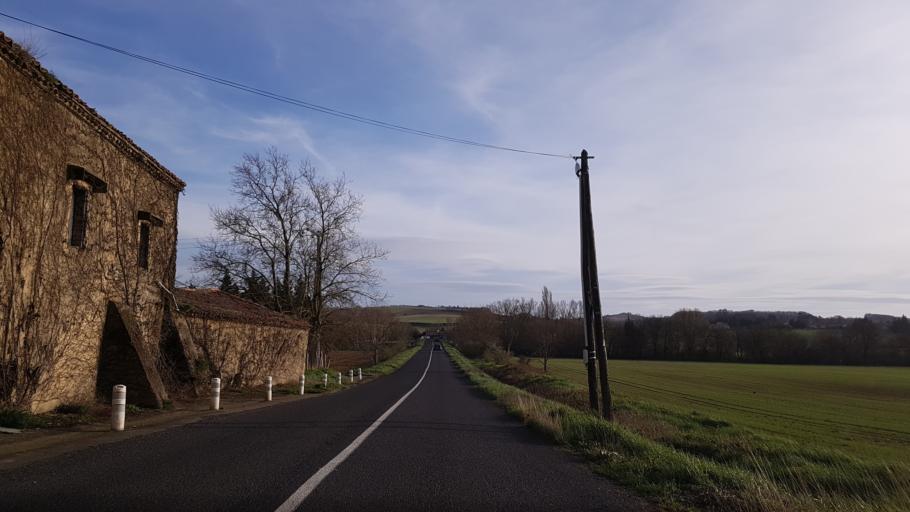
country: FR
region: Languedoc-Roussillon
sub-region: Departement de l'Aude
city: Villeneuve-la-Comptal
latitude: 43.1906
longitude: 1.9028
